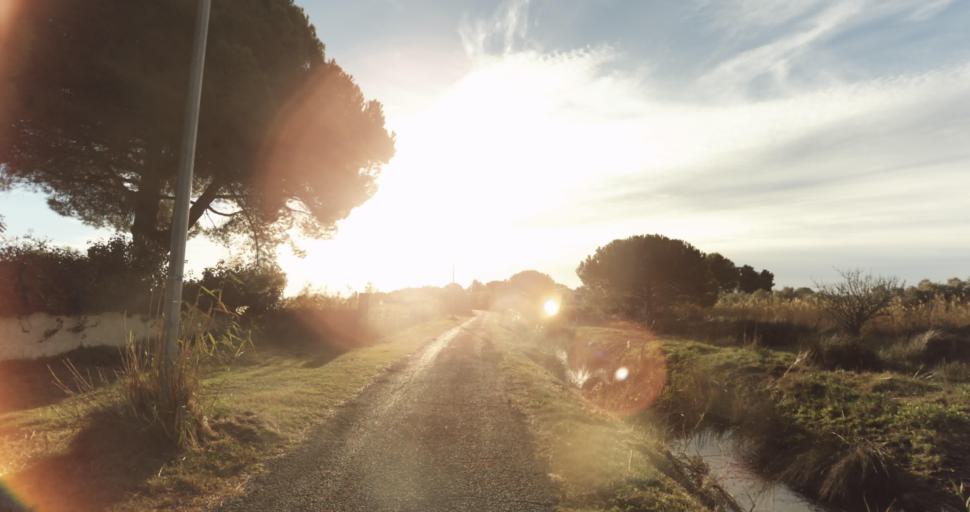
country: FR
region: Languedoc-Roussillon
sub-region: Departement du Gard
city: Aigues-Mortes
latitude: 43.5617
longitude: 4.1986
